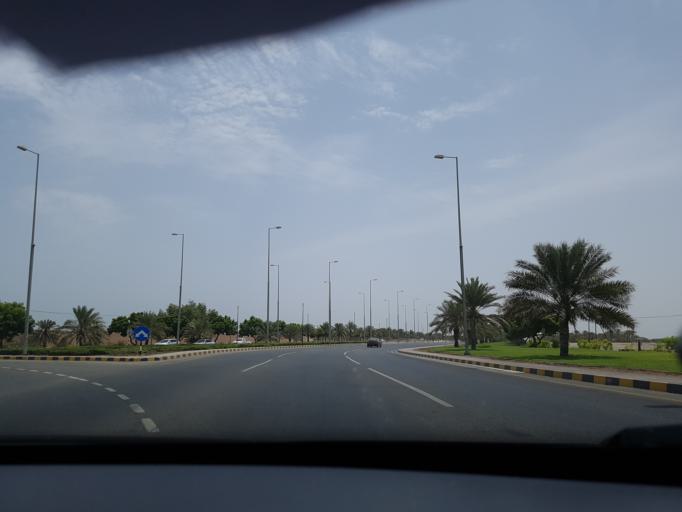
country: OM
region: Muhafazat Masqat
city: As Sib al Jadidah
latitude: 23.6898
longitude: 58.0816
